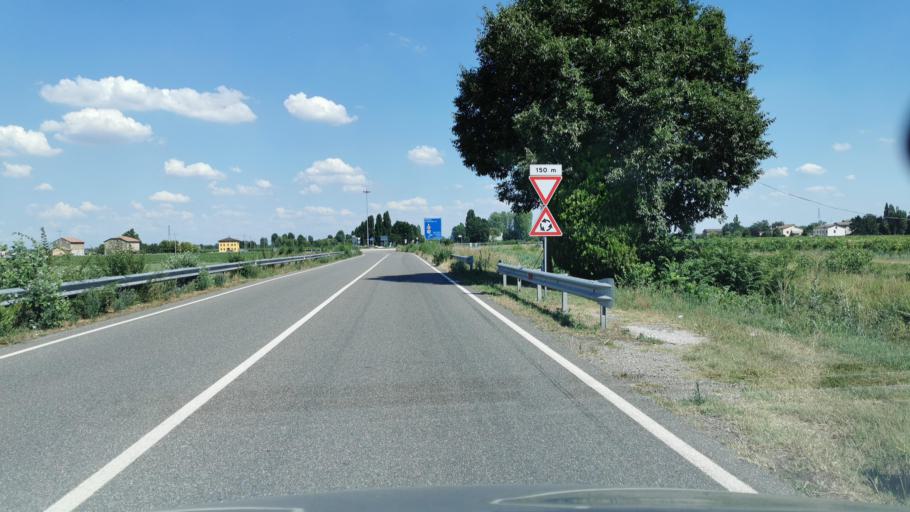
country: IT
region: Emilia-Romagna
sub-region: Provincia di Modena
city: Sam Marino
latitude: 44.7984
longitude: 10.9128
